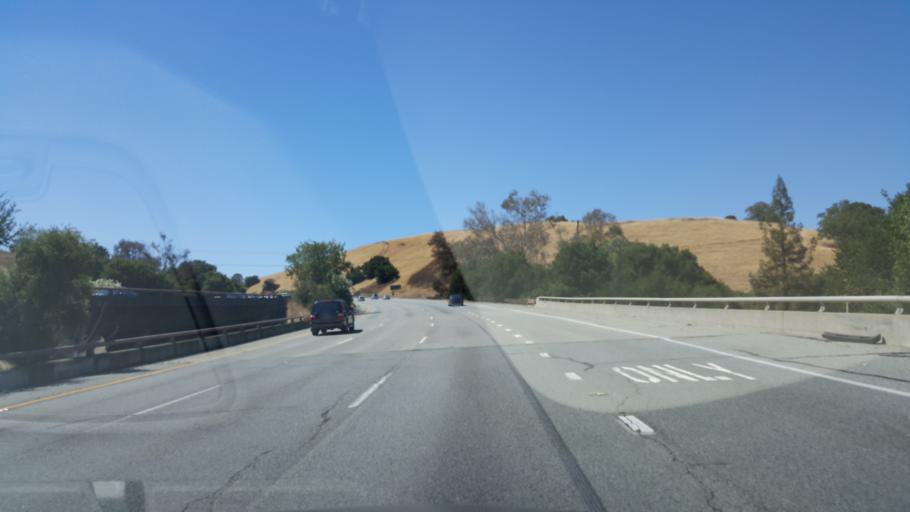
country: US
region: California
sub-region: Santa Clara County
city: Los Altos Hills
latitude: 37.3861
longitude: -122.1530
